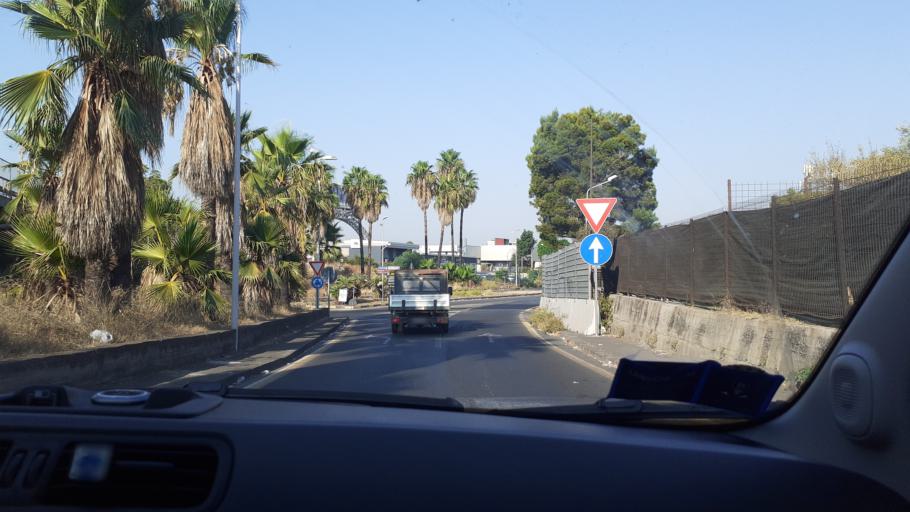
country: IT
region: Sicily
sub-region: Catania
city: Misterbianco
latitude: 37.5115
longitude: 15.0356
